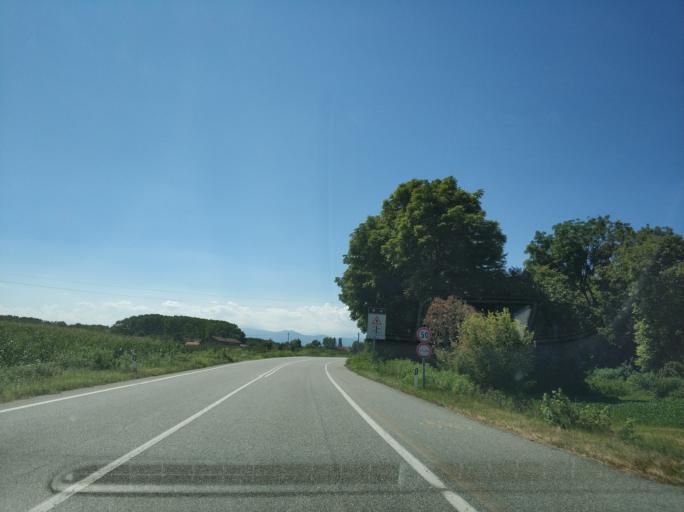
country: IT
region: Piedmont
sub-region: Provincia di Torino
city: Brandizzo
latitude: 45.2072
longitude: 7.8263
